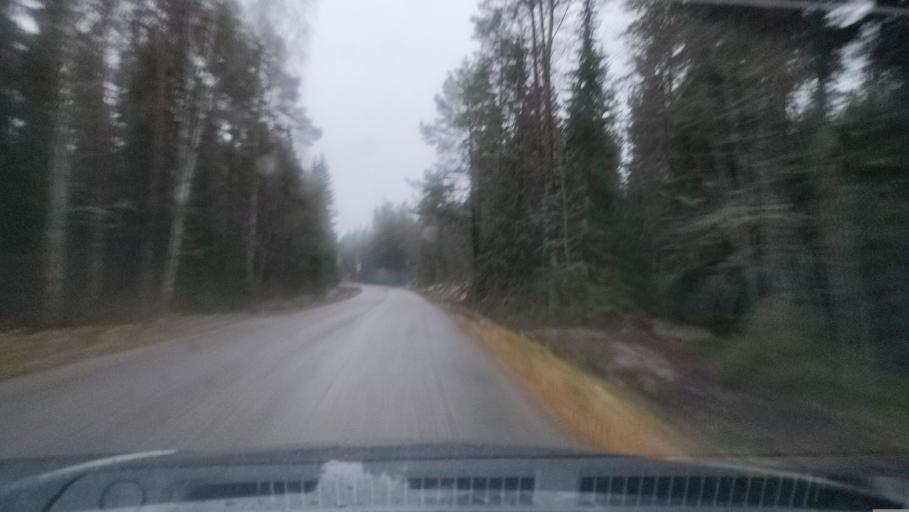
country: FI
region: Southern Ostrobothnia
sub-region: Suupohja
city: Karijoki
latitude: 62.1336
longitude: 21.5758
